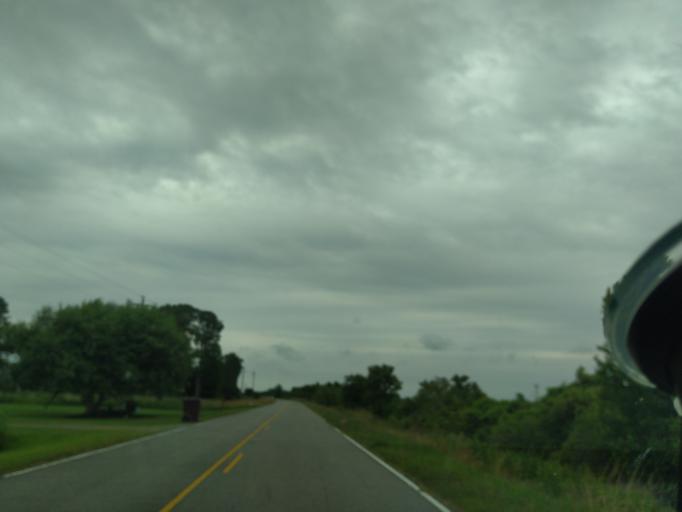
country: US
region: North Carolina
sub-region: Beaufort County
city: Belhaven
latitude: 35.7531
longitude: -76.5121
